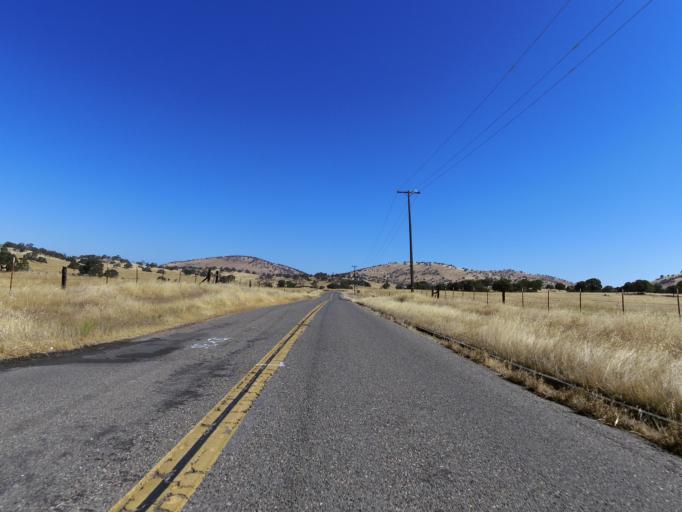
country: US
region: California
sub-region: Merced County
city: Planada
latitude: 37.6013
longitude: -120.3071
